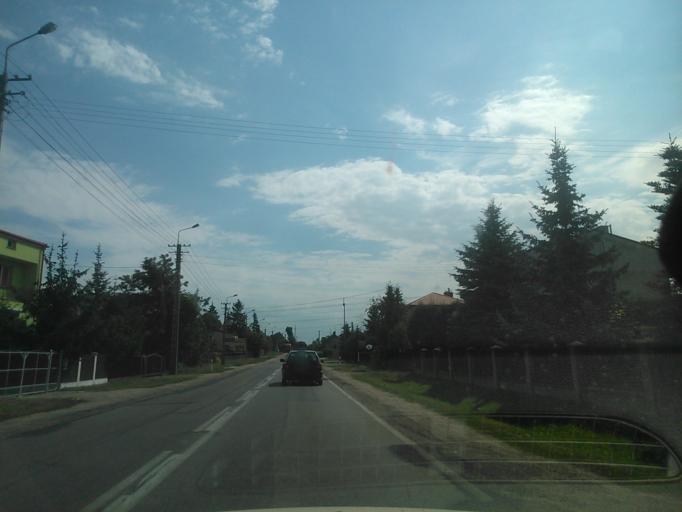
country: PL
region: Masovian Voivodeship
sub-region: Powiat mlawski
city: Mlawa
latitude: 53.1313
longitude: 20.3450
